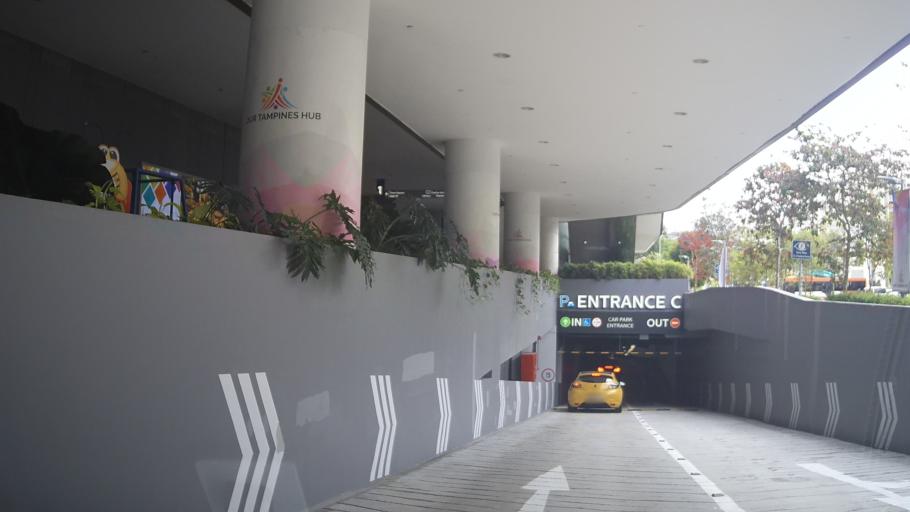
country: SG
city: Singapore
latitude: 1.3519
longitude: 103.9404
